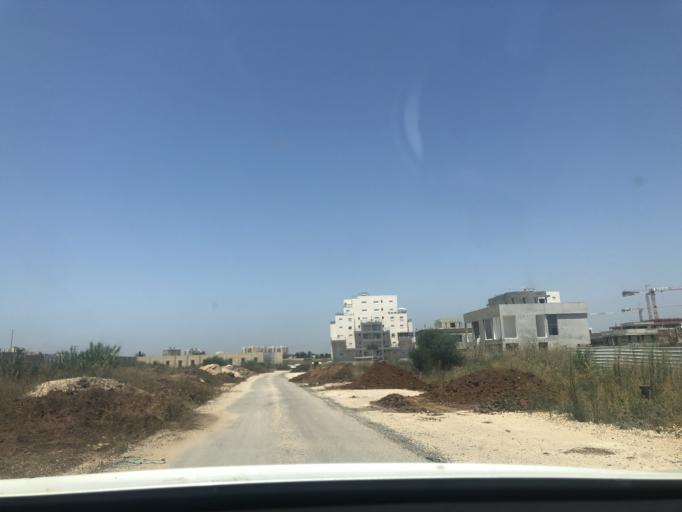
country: IL
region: Central District
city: Lod
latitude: 31.9355
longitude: 34.8946
